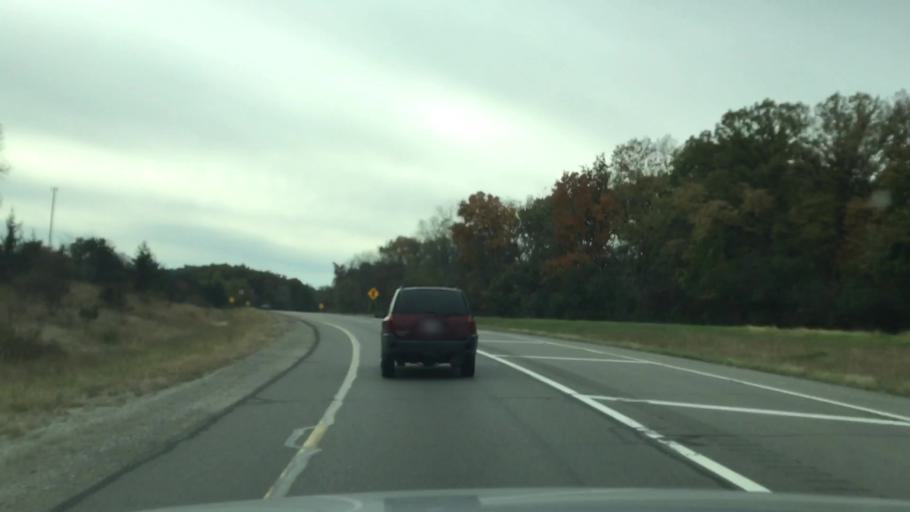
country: US
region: Michigan
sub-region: Washtenaw County
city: Ann Arbor
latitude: 42.3188
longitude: -83.7404
